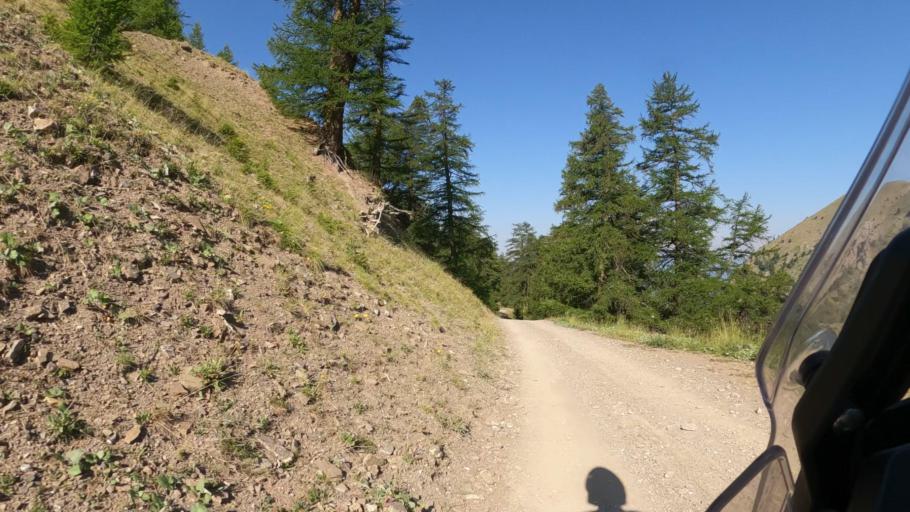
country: FR
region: Provence-Alpes-Cote d'Azur
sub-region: Departement des Hautes-Alpes
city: Guillestre
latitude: 44.5896
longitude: 6.6305
